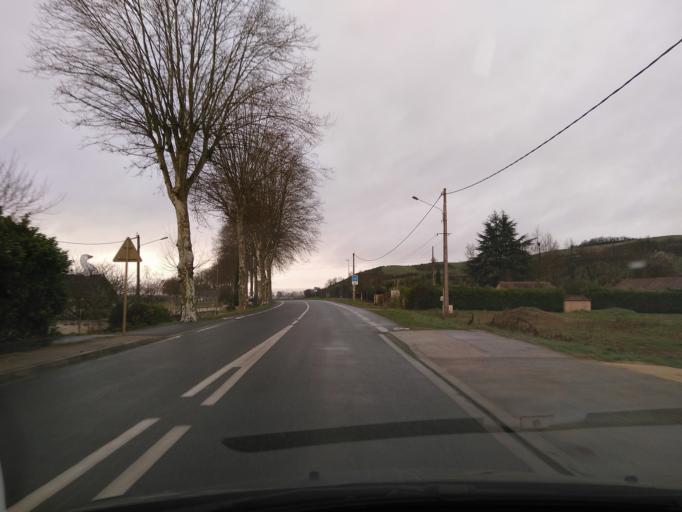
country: FR
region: Midi-Pyrenees
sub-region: Departement de la Haute-Garonne
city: Montesquieu-Volvestre
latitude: 43.2190
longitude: 1.2186
